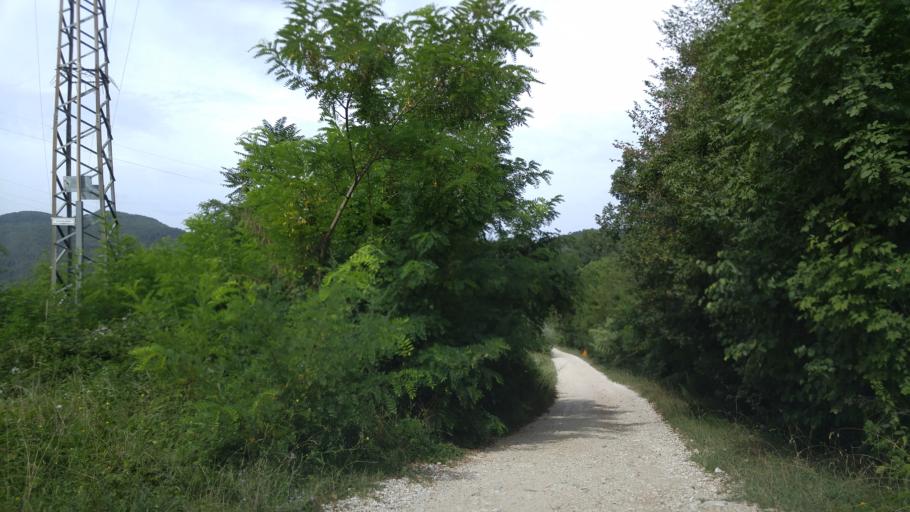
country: IT
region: The Marches
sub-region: Provincia di Pesaro e Urbino
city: Fossombrone
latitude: 43.6661
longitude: 12.7586
